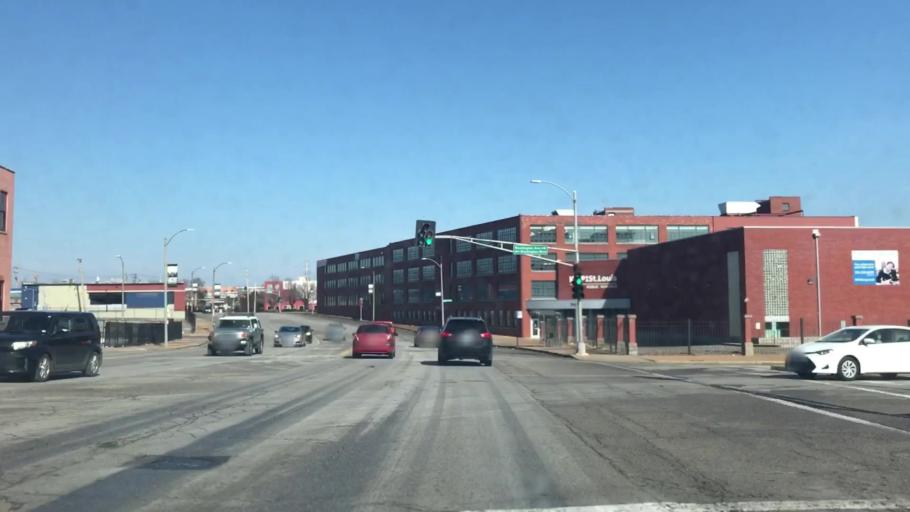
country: US
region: Missouri
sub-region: City of Saint Louis
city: St. Louis
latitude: 38.6350
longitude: -90.2132
